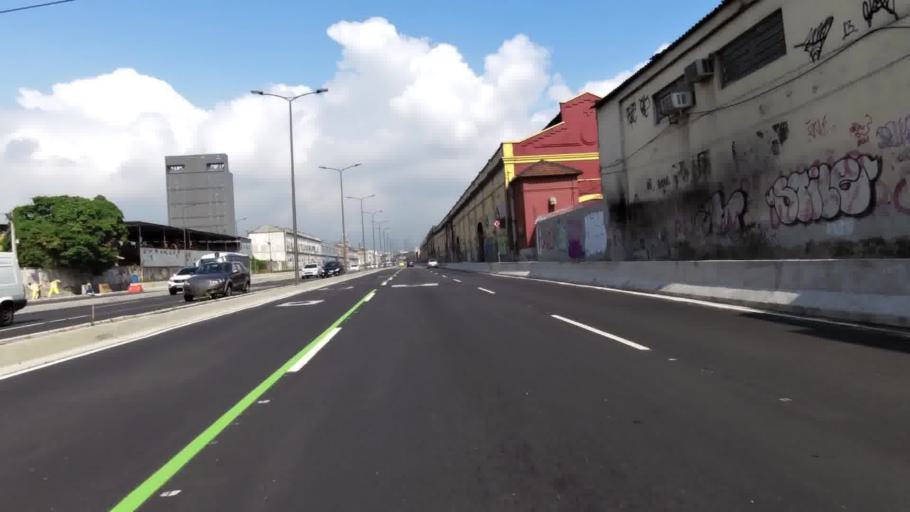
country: BR
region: Rio de Janeiro
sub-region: Rio De Janeiro
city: Rio de Janeiro
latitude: -22.8956
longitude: -43.2031
